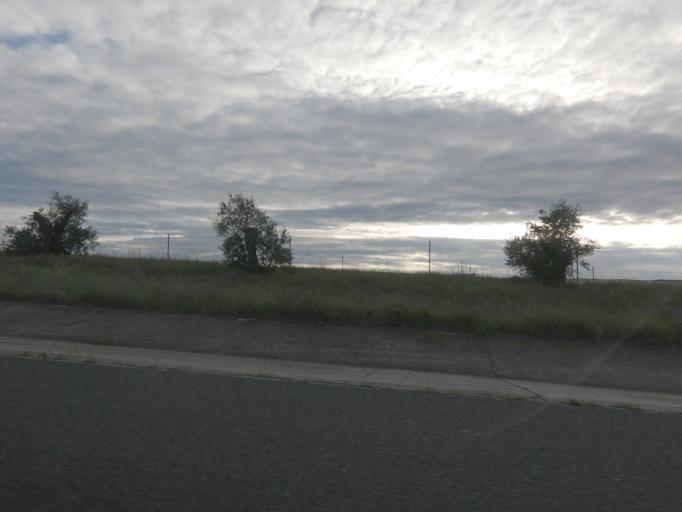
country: ES
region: Extremadura
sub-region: Provincia de Caceres
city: Casar de Caceres
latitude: 39.5657
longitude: -6.4011
